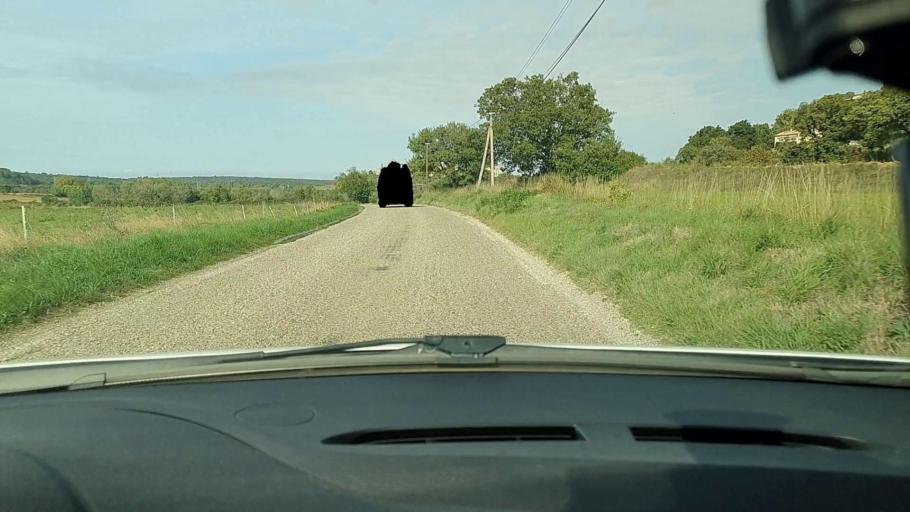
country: FR
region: Languedoc-Roussillon
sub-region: Departement du Gard
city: Goudargues
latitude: 44.1470
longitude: 4.3795
